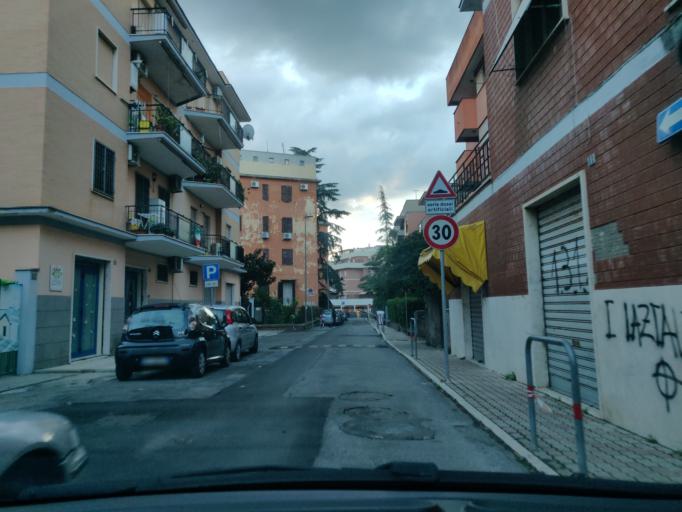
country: IT
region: Latium
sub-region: Citta metropolitana di Roma Capitale
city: Civitavecchia
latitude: 42.0929
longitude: 11.8054
